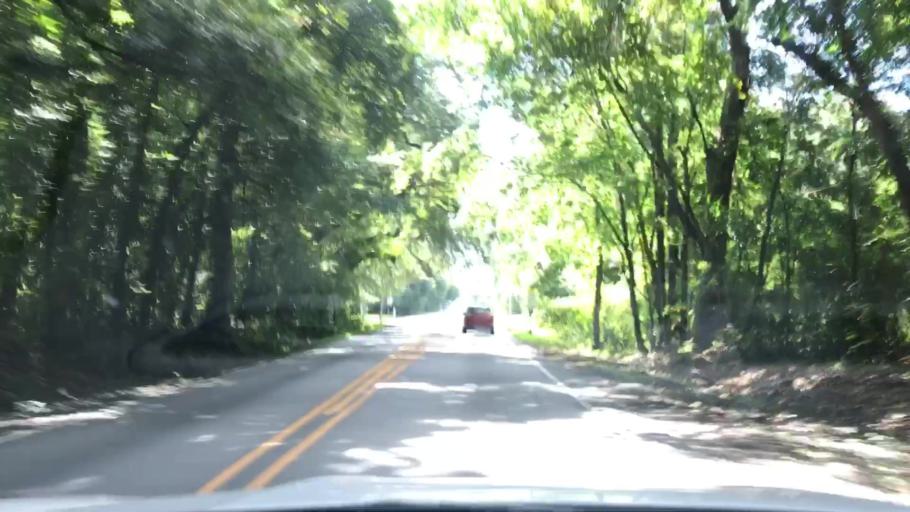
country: US
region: South Carolina
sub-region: Charleston County
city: Shell Point
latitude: 32.8566
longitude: -80.0735
